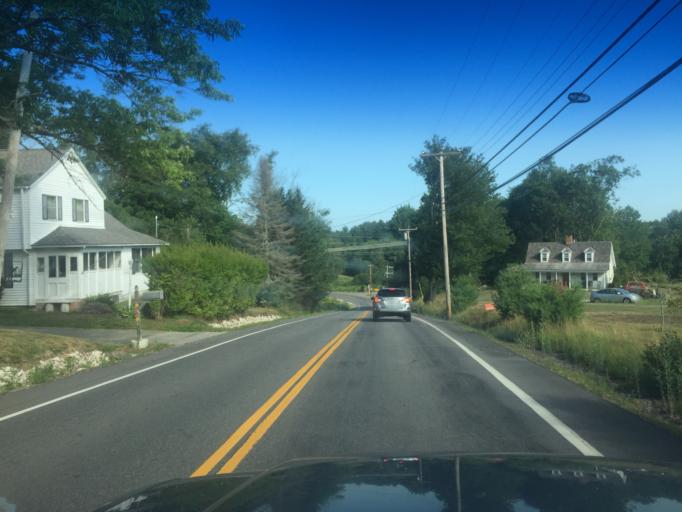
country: US
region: Maine
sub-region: York County
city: South Berwick
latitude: 43.2106
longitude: -70.7855
